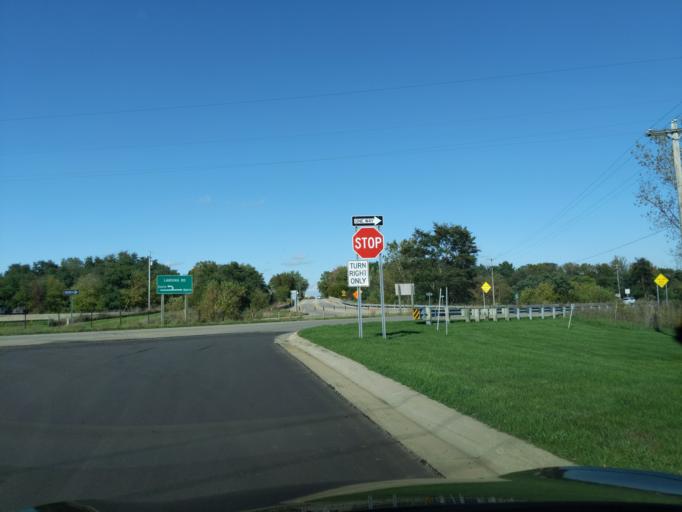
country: US
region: Michigan
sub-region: Eaton County
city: Charlotte
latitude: 42.5880
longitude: -84.7979
